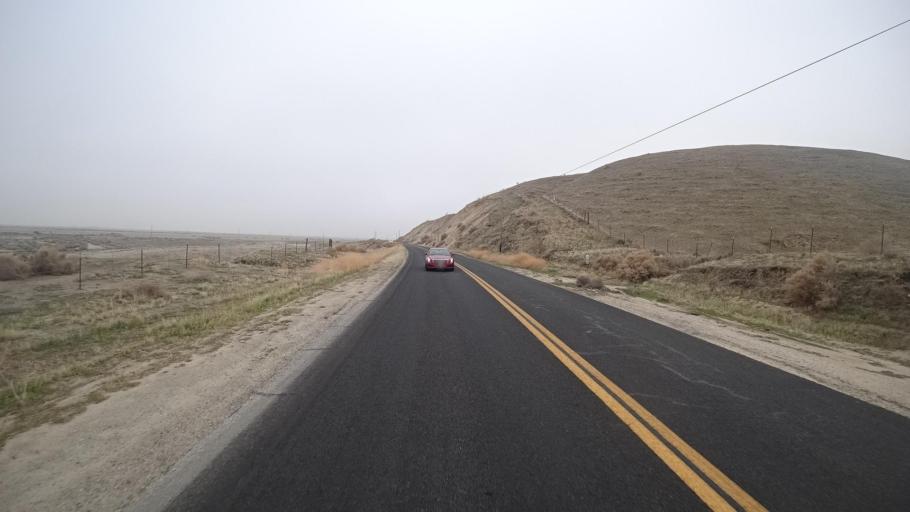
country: US
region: California
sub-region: Kern County
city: Ford City
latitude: 35.2573
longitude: -119.3092
